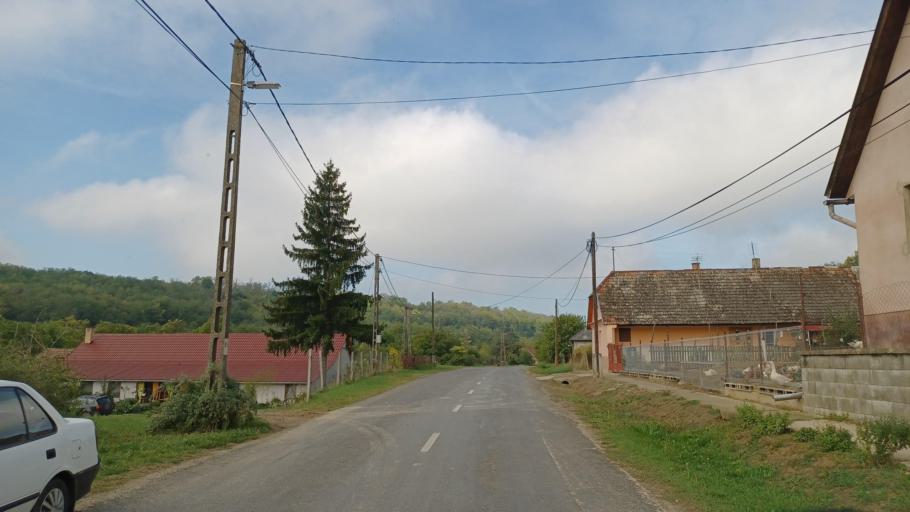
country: HU
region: Tolna
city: Pincehely
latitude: 46.6469
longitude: 18.5231
